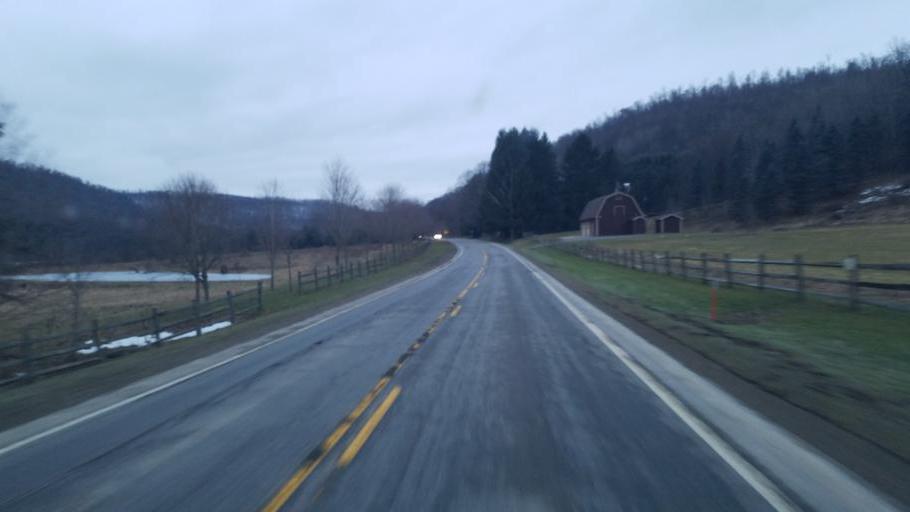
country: US
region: Pennsylvania
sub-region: Potter County
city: Coudersport
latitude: 41.8346
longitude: -77.9452
